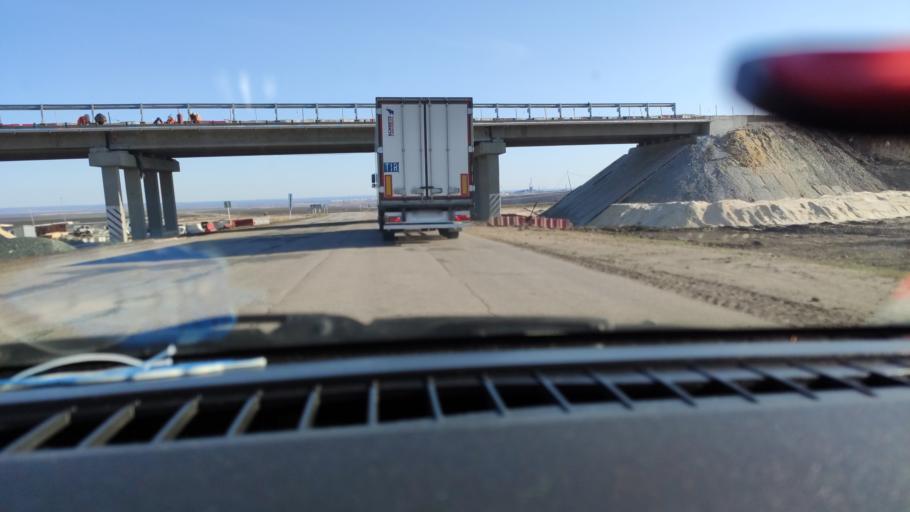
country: RU
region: Samara
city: Syzran'
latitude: 53.0005
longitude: 48.3294
